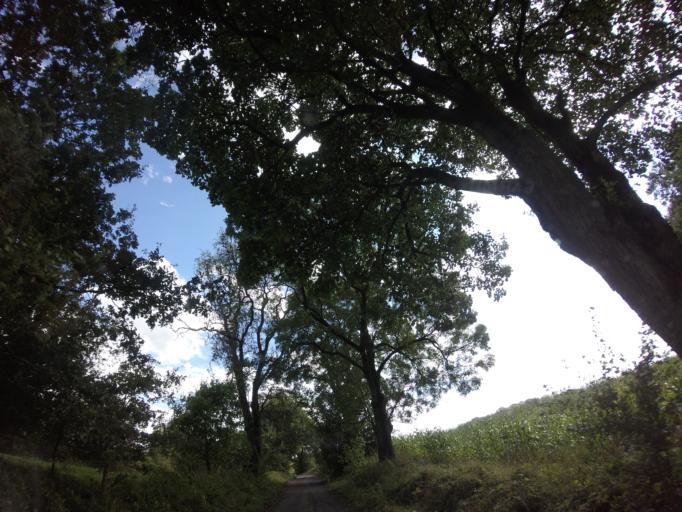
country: PL
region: West Pomeranian Voivodeship
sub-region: Powiat choszczenski
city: Recz
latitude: 53.2883
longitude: 15.5958
